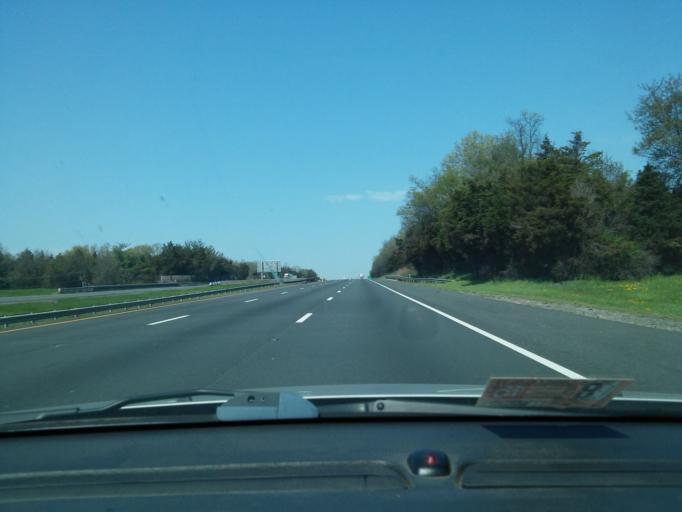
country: US
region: New Jersey
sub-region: Somerset County
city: Bedminster
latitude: 40.6431
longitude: -74.6872
